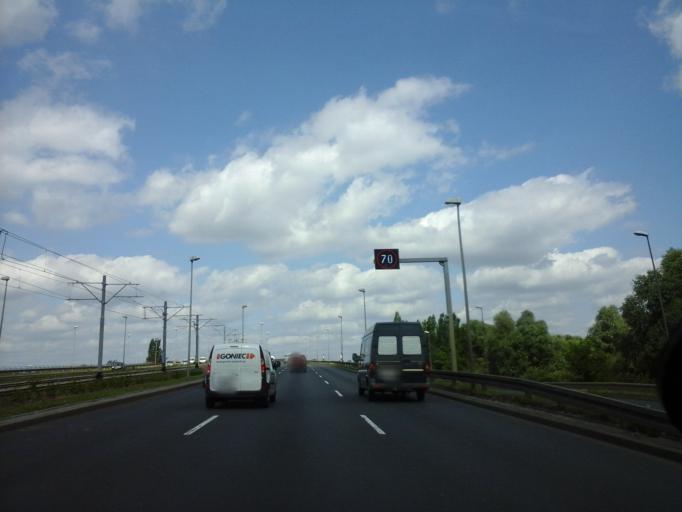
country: PL
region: West Pomeranian Voivodeship
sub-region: Szczecin
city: Szczecin
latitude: 53.3914
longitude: 14.6185
